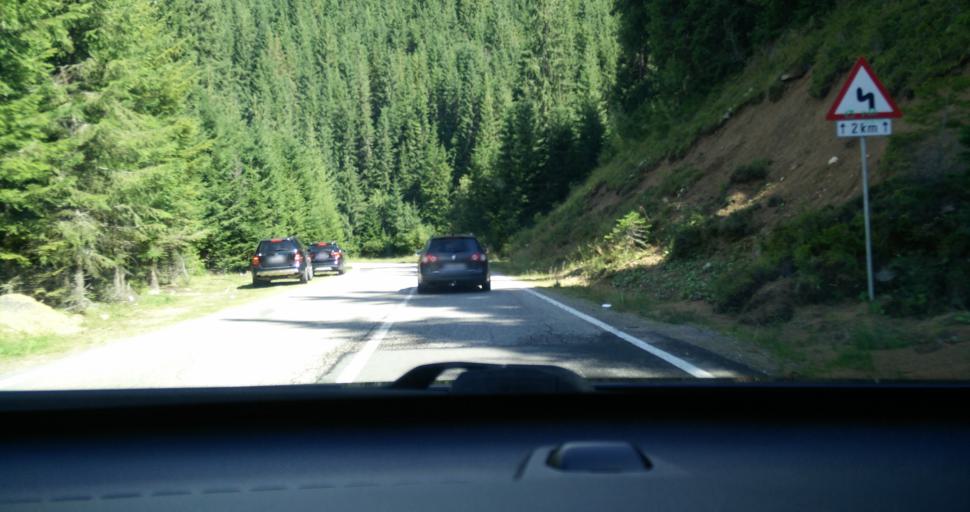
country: RO
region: Alba
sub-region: Comuna Sugag
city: Sugag
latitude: 45.5438
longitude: 23.6376
